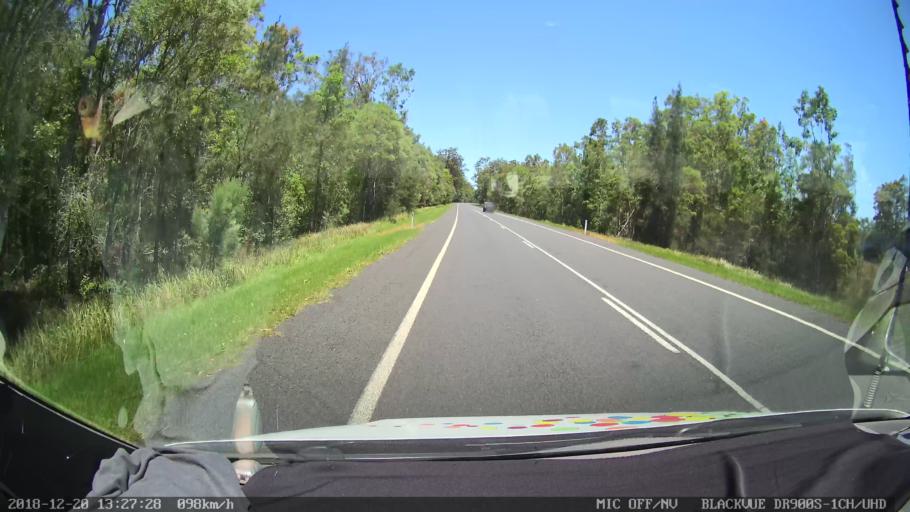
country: AU
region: New South Wales
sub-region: Richmond Valley
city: Casino
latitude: -29.1605
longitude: 152.9920
